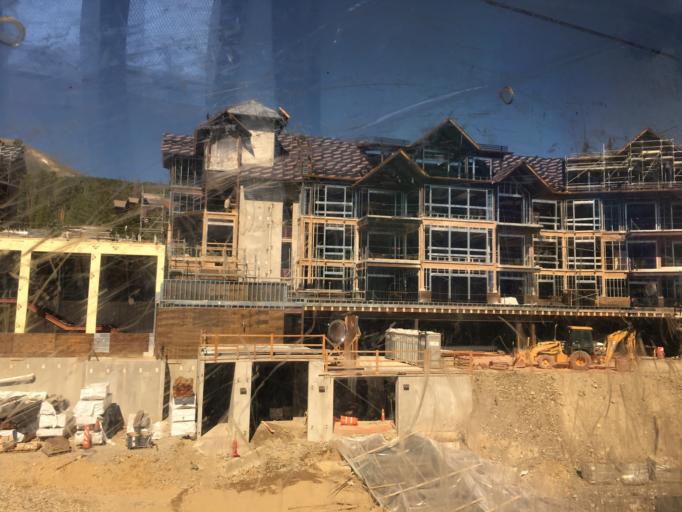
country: US
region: Colorado
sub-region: Summit County
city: Breckenridge
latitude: 39.4820
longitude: -106.0670
